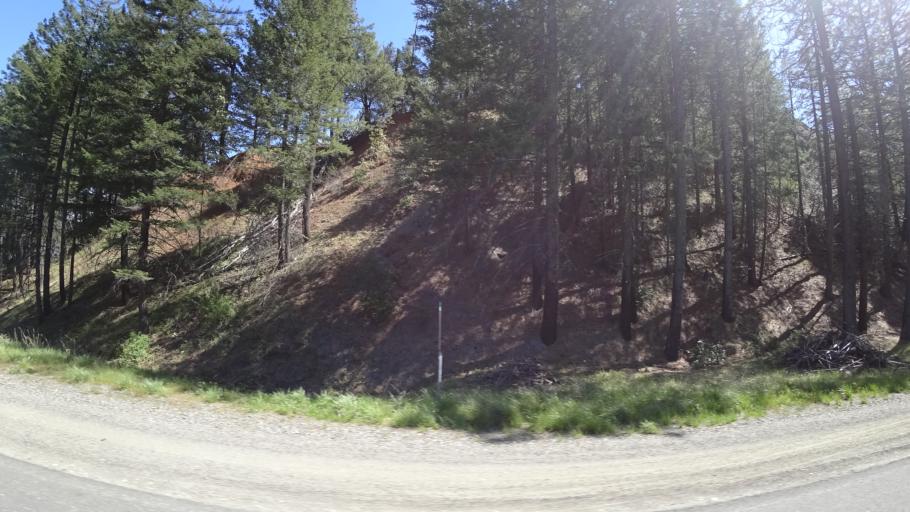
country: US
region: California
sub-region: Trinity County
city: Weaverville
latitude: 40.7386
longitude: -122.9830
